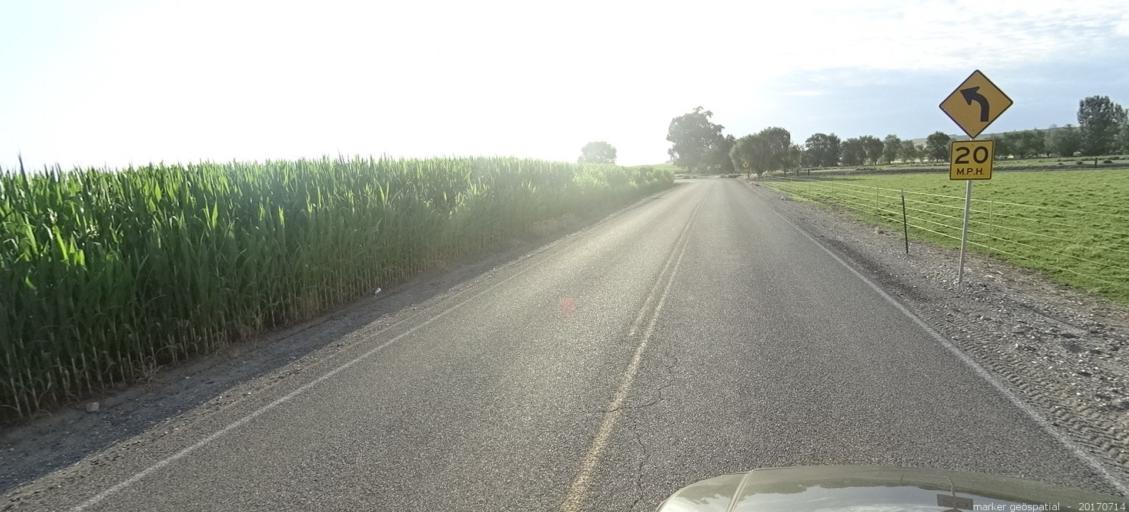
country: US
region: Idaho
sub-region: Ada County
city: Kuna
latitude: 43.4592
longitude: -116.4967
